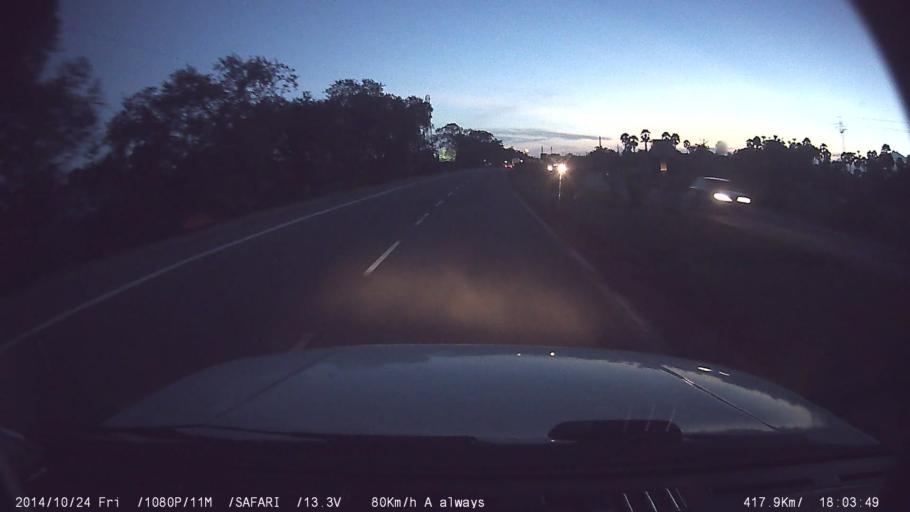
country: IN
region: Tamil Nadu
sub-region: Kancheepuram
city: Chengalpattu
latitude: 12.6164
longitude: 79.9262
